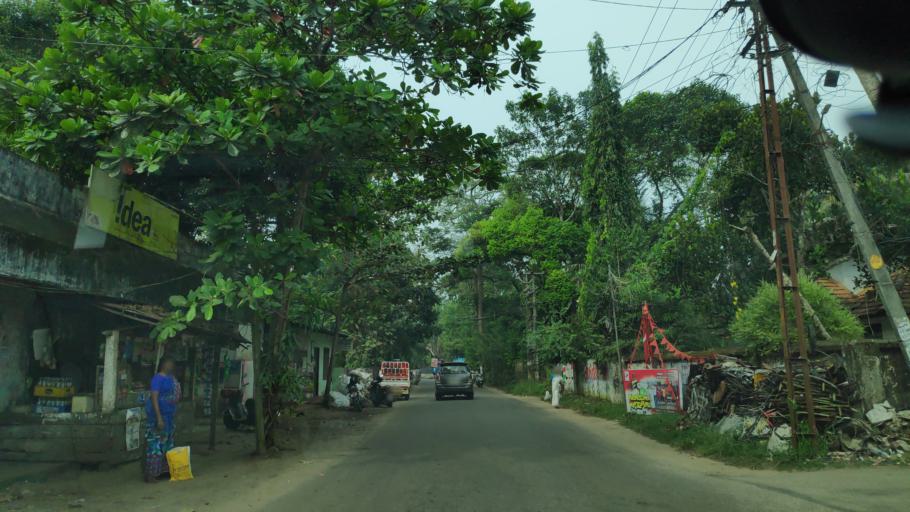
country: IN
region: Kerala
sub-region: Alappuzha
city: Alleppey
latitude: 9.5706
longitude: 76.3289
